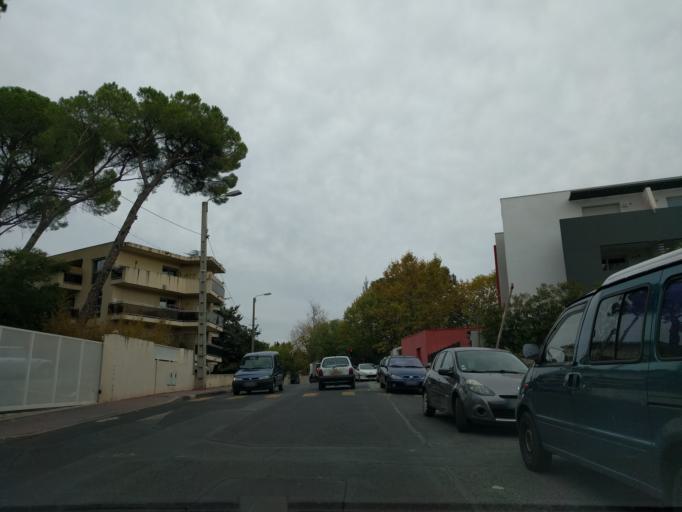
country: FR
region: Languedoc-Roussillon
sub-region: Departement de l'Herault
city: Montpellier
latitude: 43.6340
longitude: 3.8729
